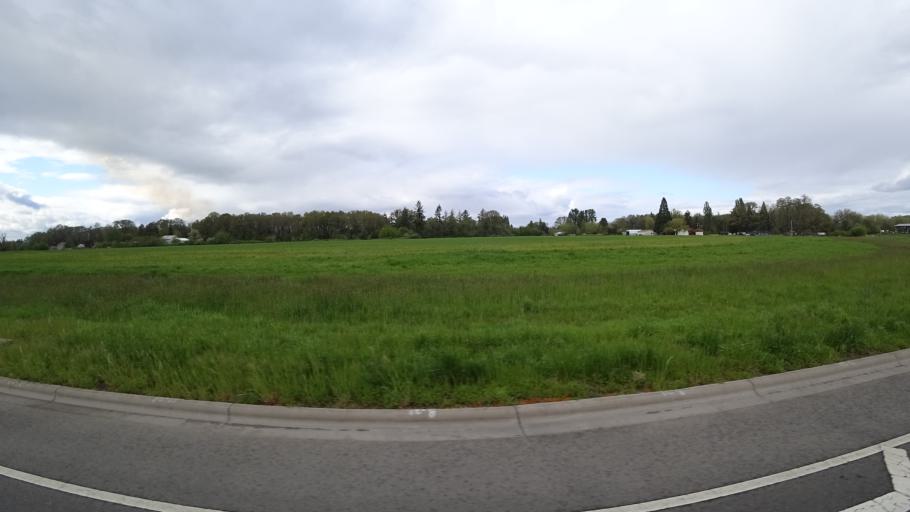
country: US
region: Oregon
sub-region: Washington County
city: Hillsboro
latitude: 45.5515
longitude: -122.9559
